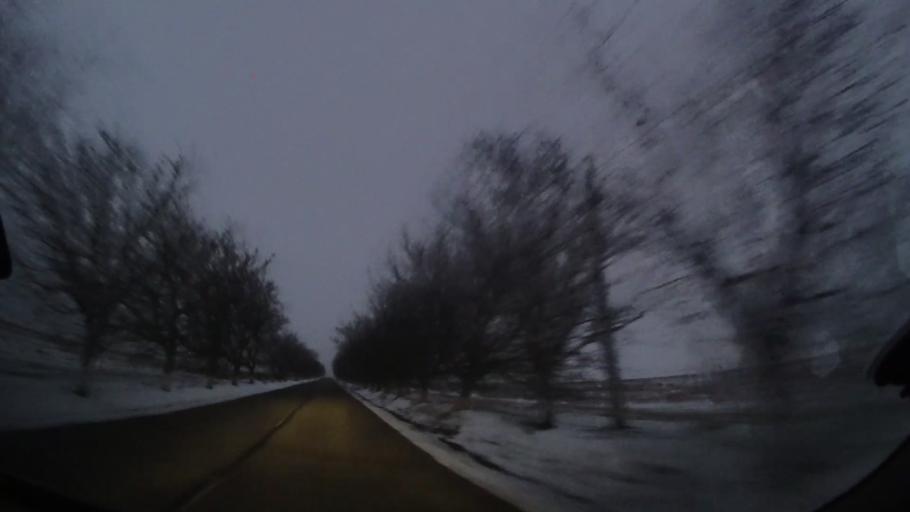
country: RO
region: Vaslui
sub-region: Comuna Hoceni
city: Hoceni
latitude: 46.5195
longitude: 28.0277
